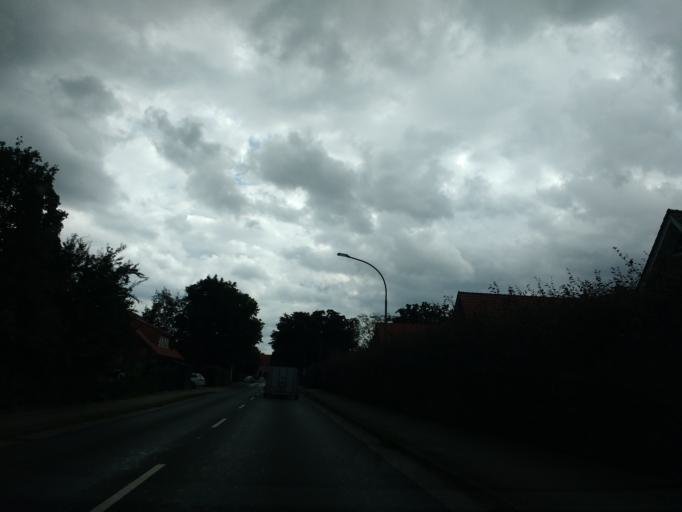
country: DE
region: Lower Saxony
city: Glandorf
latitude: 52.0836
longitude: 7.9976
